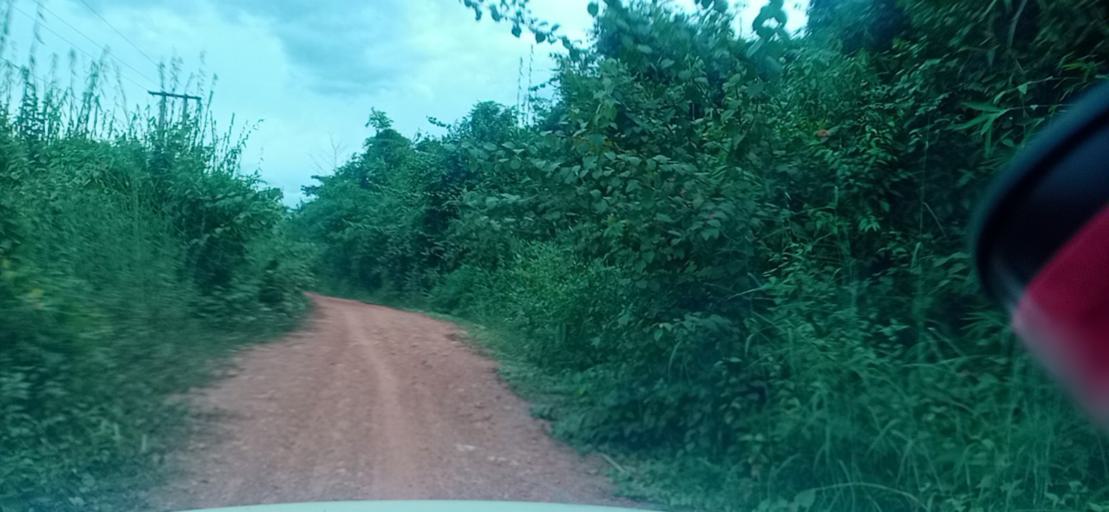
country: TH
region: Changwat Bueng Kan
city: Pak Khat
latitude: 18.5627
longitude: 103.3008
